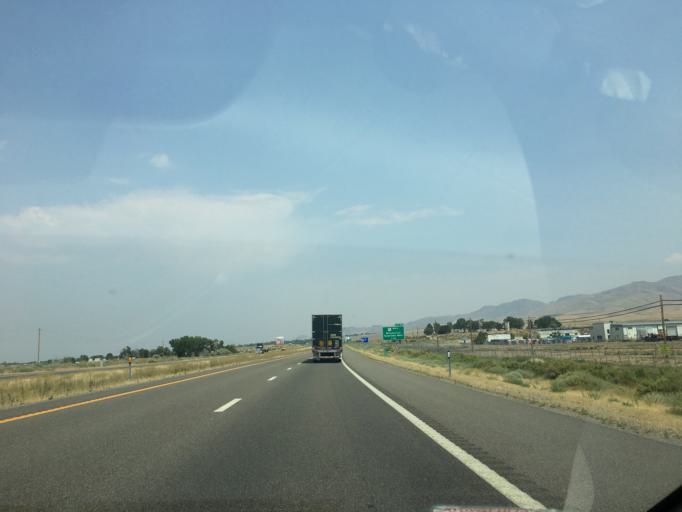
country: US
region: Nevada
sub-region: Humboldt County
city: Winnemucca
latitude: 40.9424
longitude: -117.7764
